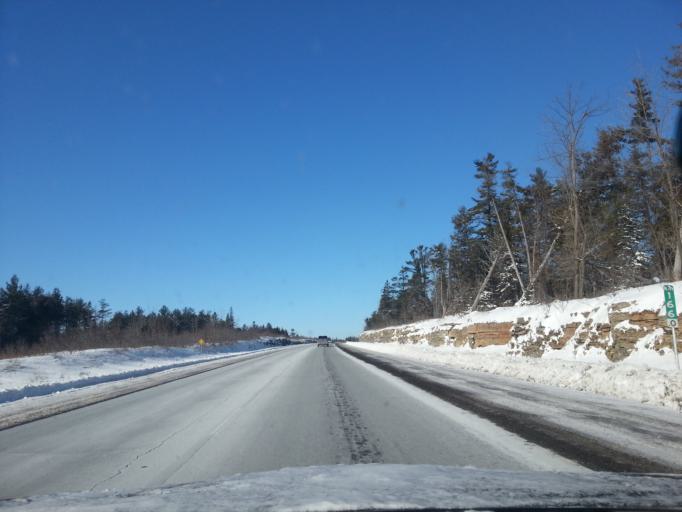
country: CA
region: Ontario
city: Arnprior
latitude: 45.3374
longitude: -76.1820
